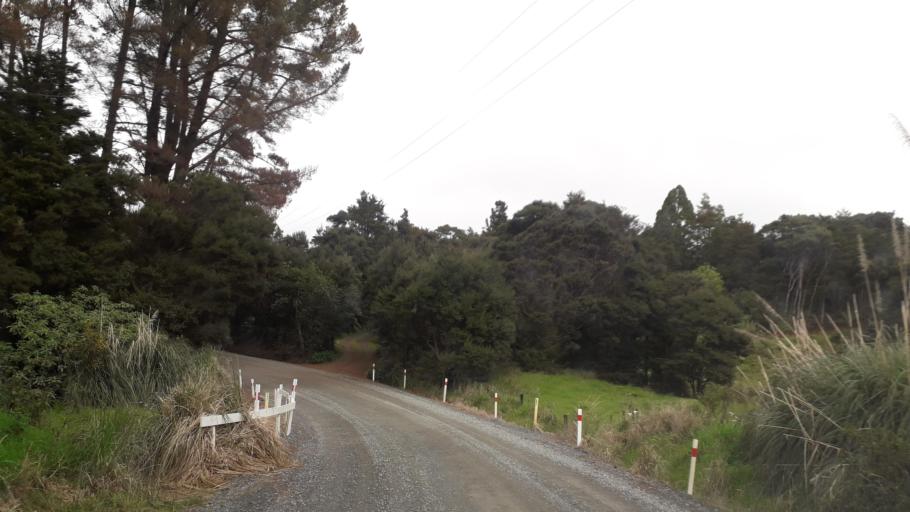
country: NZ
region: Northland
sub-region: Far North District
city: Kerikeri
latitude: -35.1181
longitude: 173.7503
